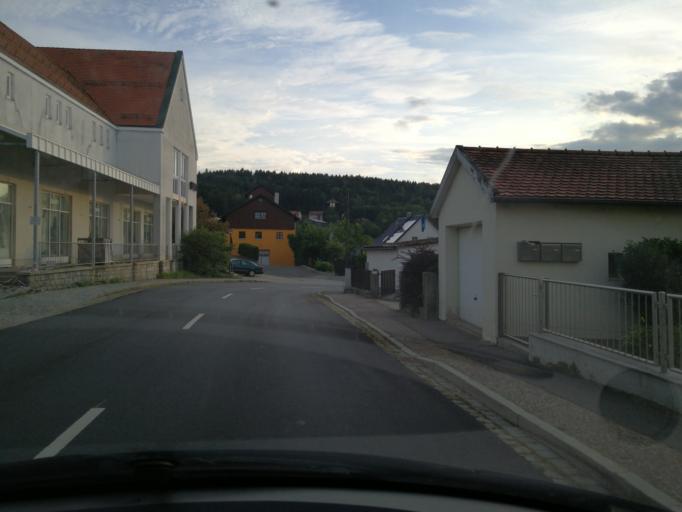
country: DE
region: Bavaria
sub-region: Upper Palatinate
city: Falkenstein
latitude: 49.0969
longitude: 12.4879
